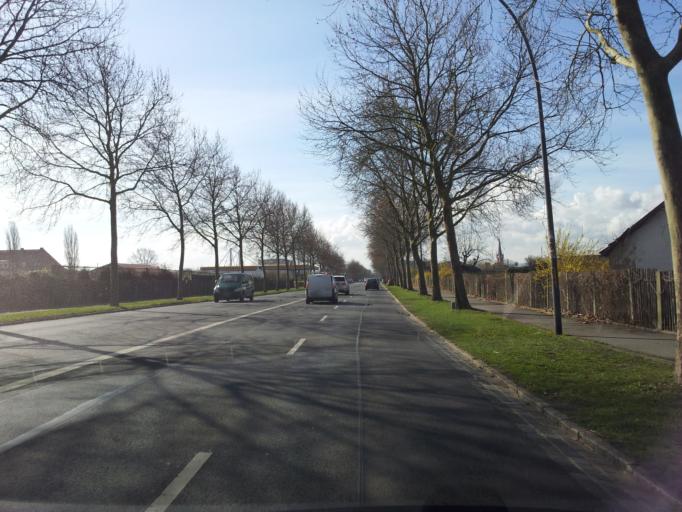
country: DE
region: Saxony
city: Albertstadt
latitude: 51.0822
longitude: 13.7394
